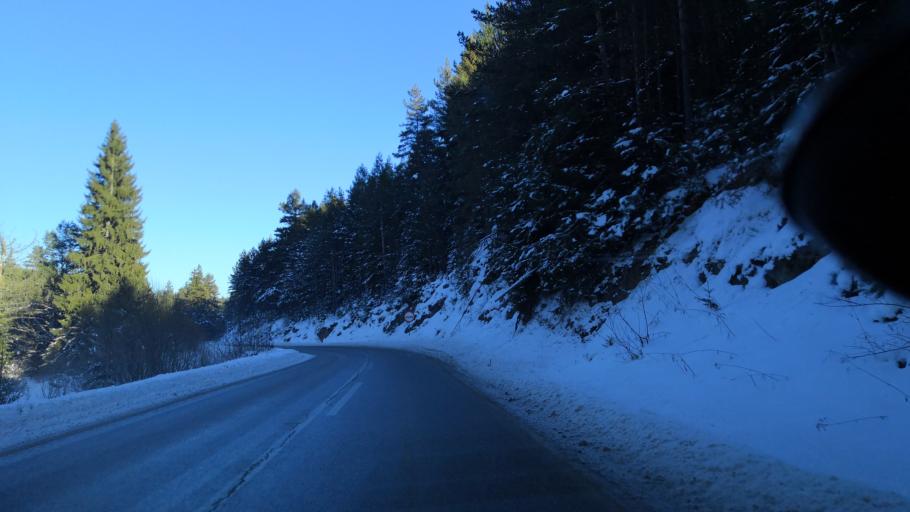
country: BA
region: Republika Srpska
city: Sokolac
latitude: 43.9867
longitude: 18.8647
